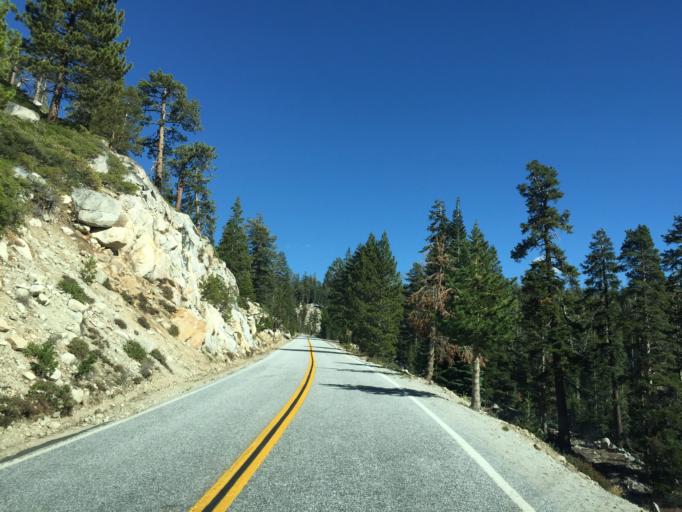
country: US
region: California
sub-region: Mariposa County
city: Yosemite Valley
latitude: 37.8172
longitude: -119.5139
